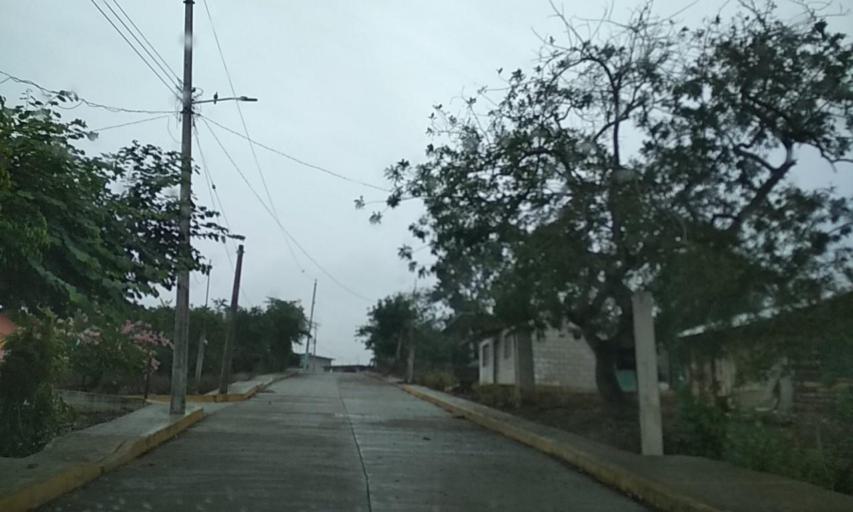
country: MX
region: Veracruz
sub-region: Papantla
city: El Chote
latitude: 20.3306
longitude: -97.3937
